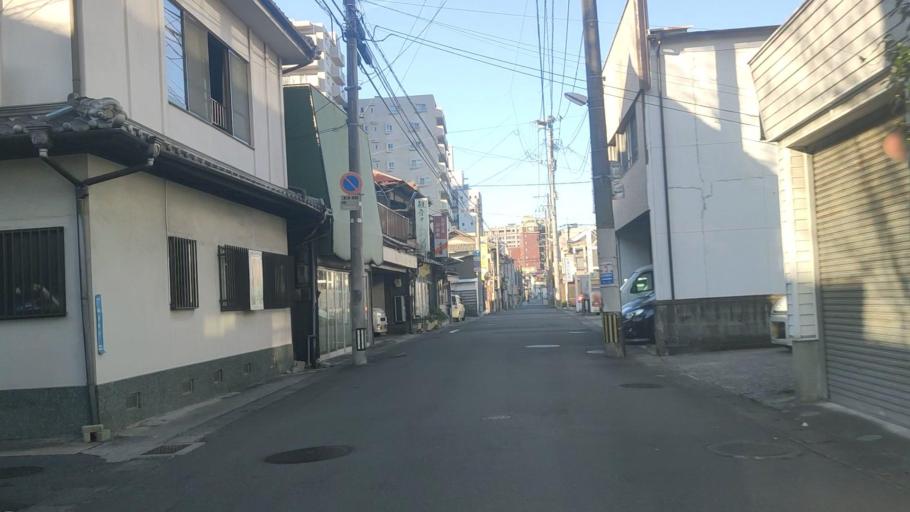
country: JP
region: Oita
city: Beppu
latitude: 33.2750
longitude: 131.5030
